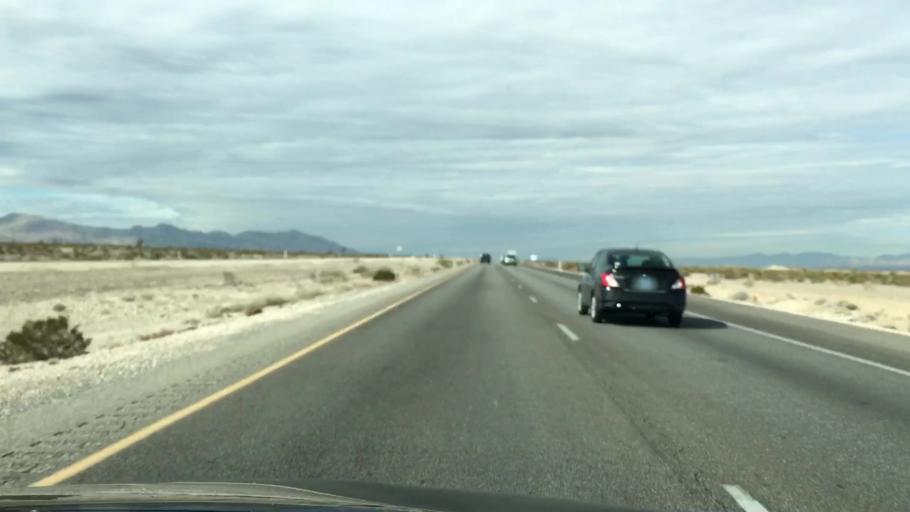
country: US
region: Nevada
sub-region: Clark County
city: Summerlin South
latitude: 36.3410
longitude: -115.3255
